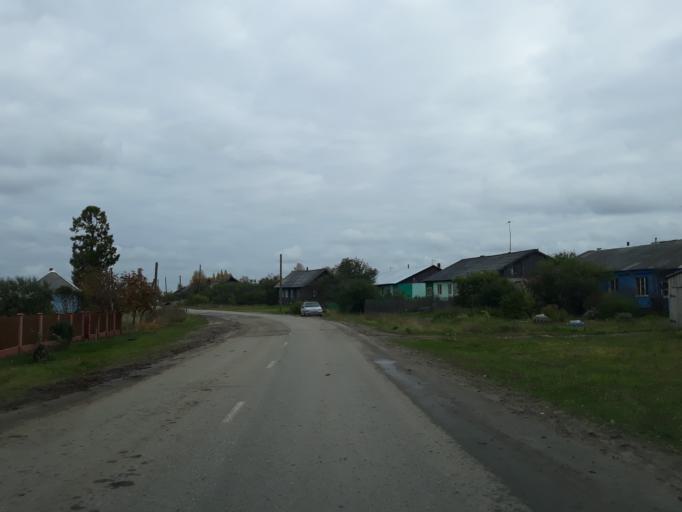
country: RU
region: Nizjnij Novgorod
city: Varnavino
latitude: 57.4287
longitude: 45.0517
